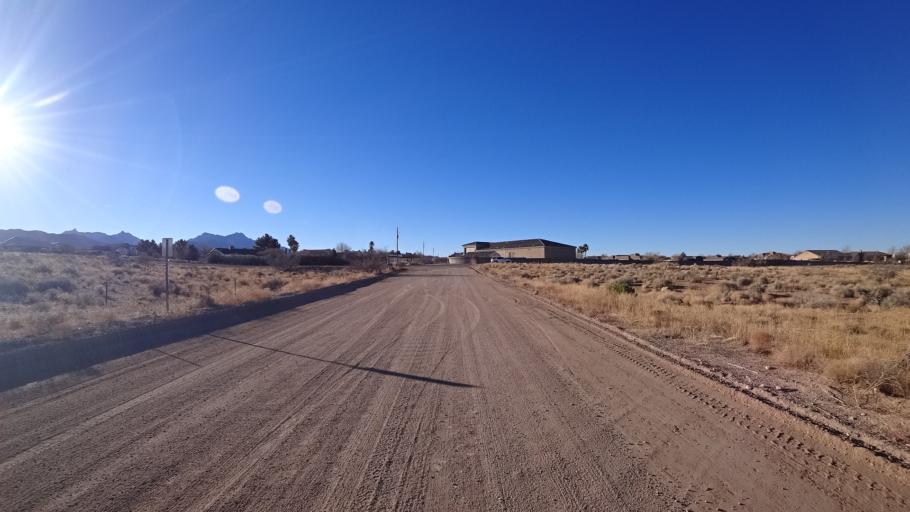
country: US
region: Arizona
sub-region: Mohave County
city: Kingman
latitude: 35.1966
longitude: -113.9939
